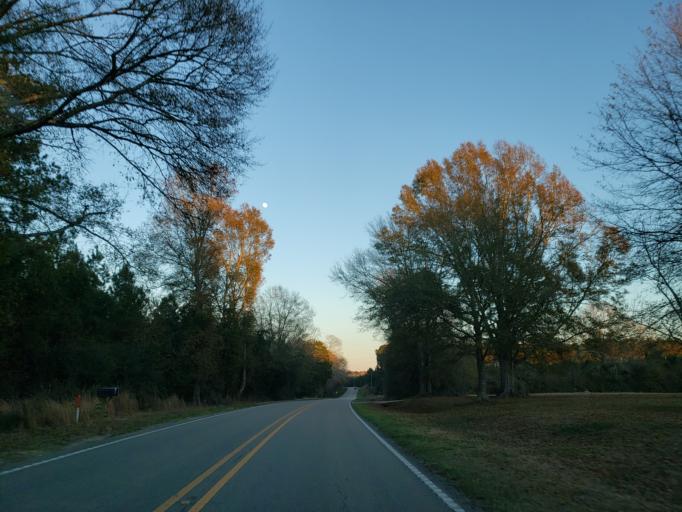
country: US
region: Mississippi
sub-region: Covington County
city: Collins
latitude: 31.5652
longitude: -89.4354
